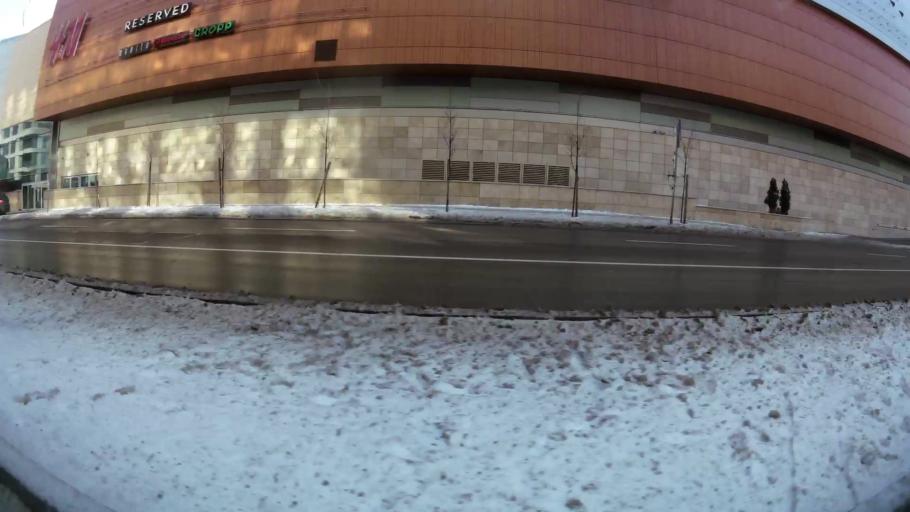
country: BG
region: Sofia-Capital
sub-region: Stolichna Obshtina
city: Sofia
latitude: 42.6585
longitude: 23.3151
